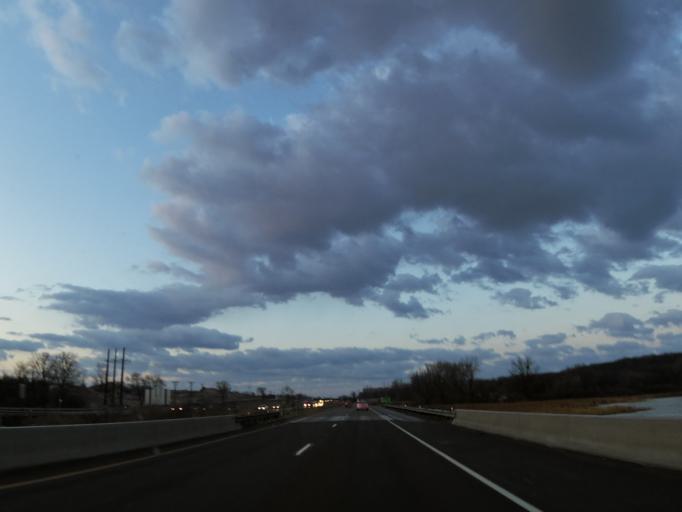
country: US
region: Minnesota
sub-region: Dakota County
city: Lakeville
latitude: 44.6732
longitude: -93.2942
